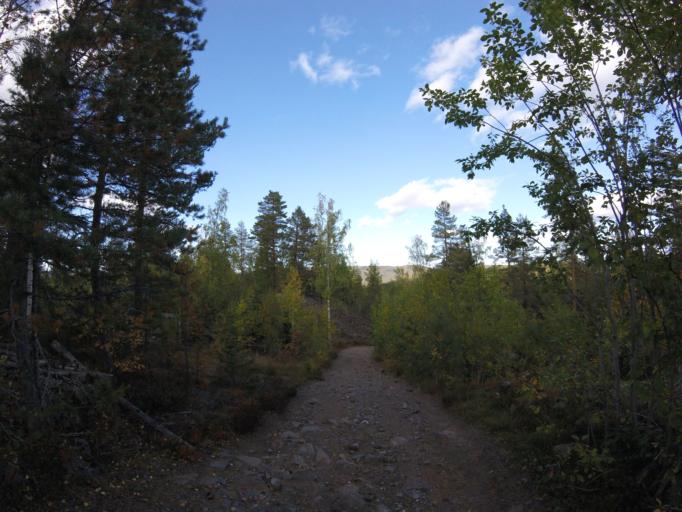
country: NO
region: Buskerud
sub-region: Kongsberg
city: Kongsberg
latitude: 59.6680
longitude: 9.6081
